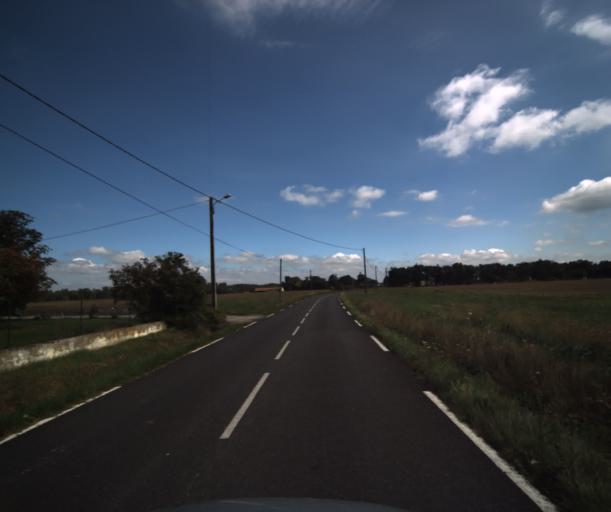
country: FR
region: Midi-Pyrenees
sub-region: Departement de la Haute-Garonne
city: Lacasse
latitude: 43.3824
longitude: 1.2459
